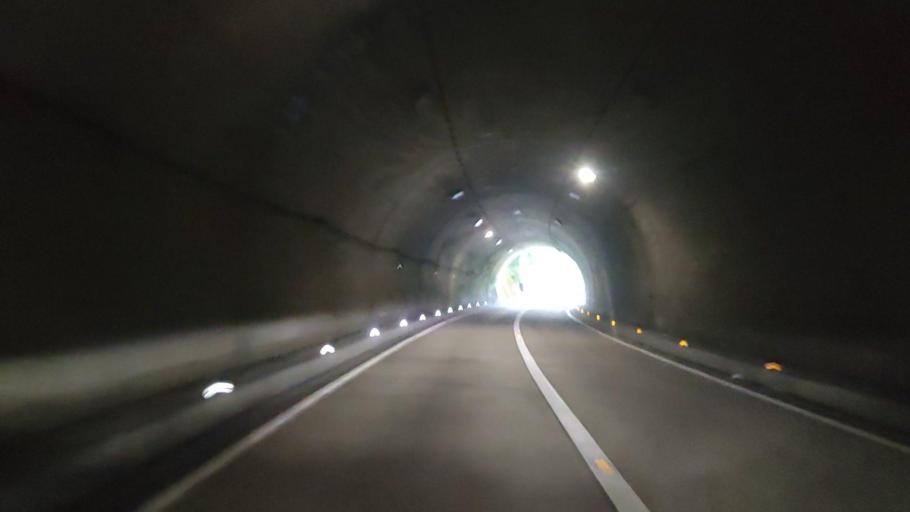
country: JP
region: Wakayama
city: Shingu
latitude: 33.8079
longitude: 135.7253
